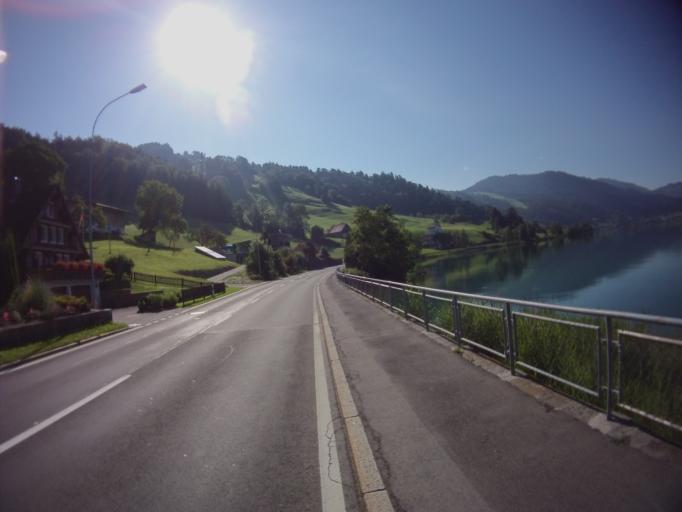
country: CH
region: Schwyz
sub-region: Bezirk Schwyz
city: Sattel
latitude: 47.1270
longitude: 8.6320
